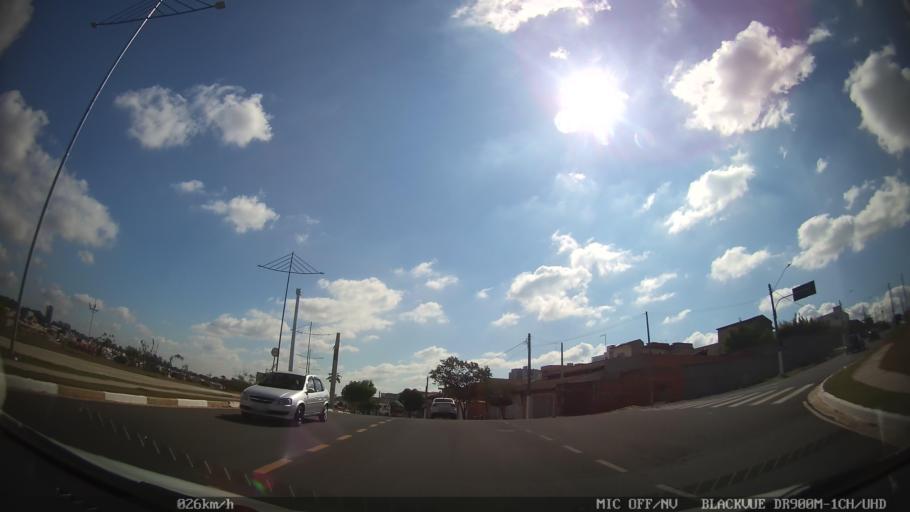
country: BR
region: Sao Paulo
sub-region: Hortolandia
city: Hortolandia
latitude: -22.8833
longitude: -47.2125
